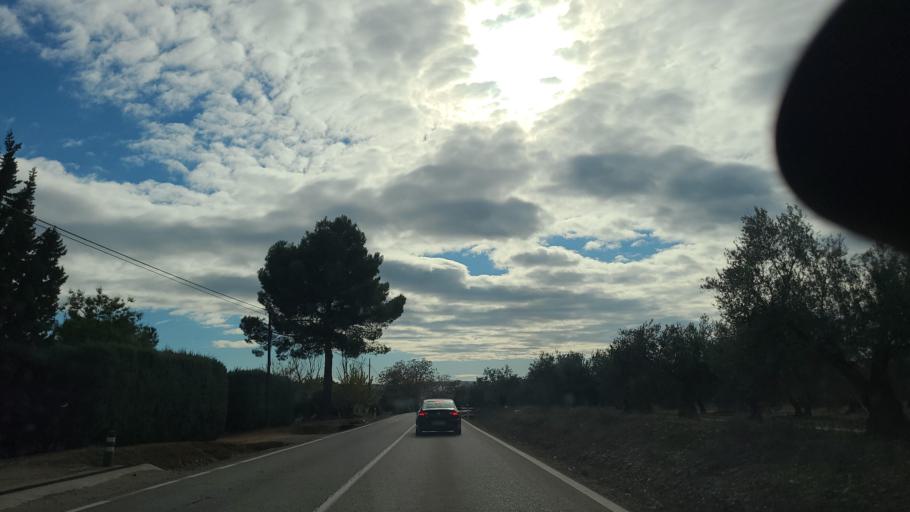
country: ES
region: Andalusia
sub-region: Provincia de Jaen
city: Villanueva de la Reina
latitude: 38.0358
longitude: -3.9162
